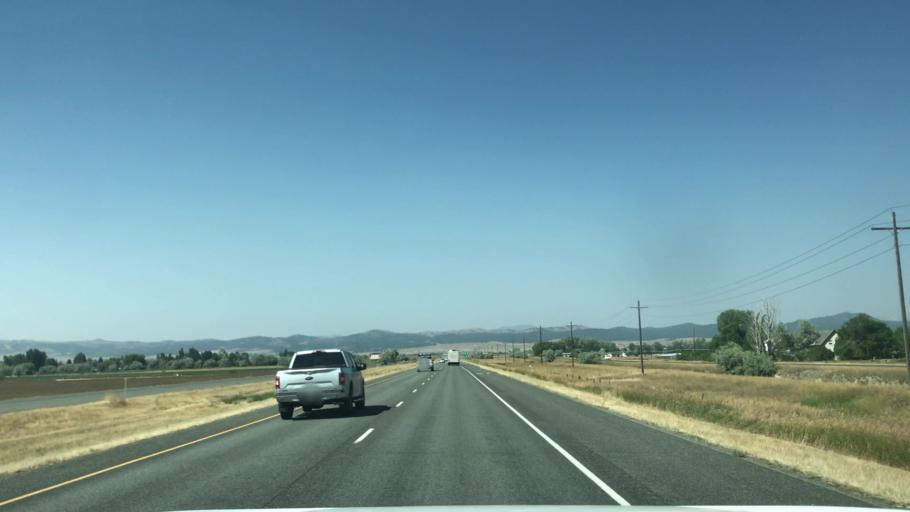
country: US
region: Montana
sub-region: Lewis and Clark County
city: Helena Valley West Central
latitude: 46.6797
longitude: -112.0115
